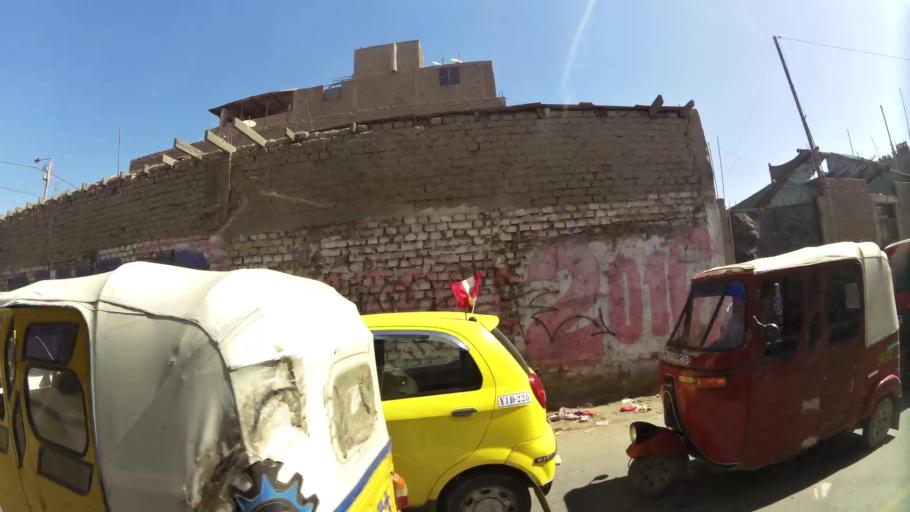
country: PE
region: Ica
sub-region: Provincia de Ica
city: Ica
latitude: -14.0624
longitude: -75.7249
